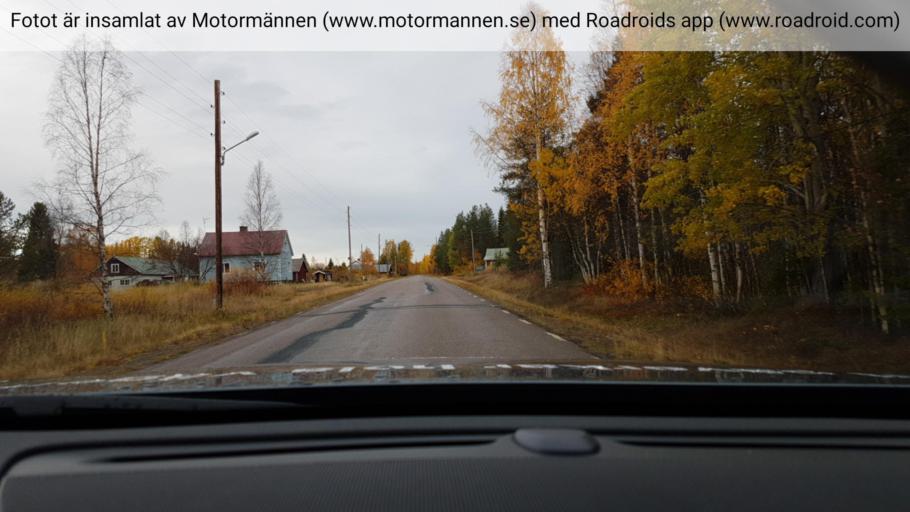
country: SE
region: Norrbotten
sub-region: Pajala Kommun
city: Pajala
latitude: 67.1704
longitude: 22.6516
